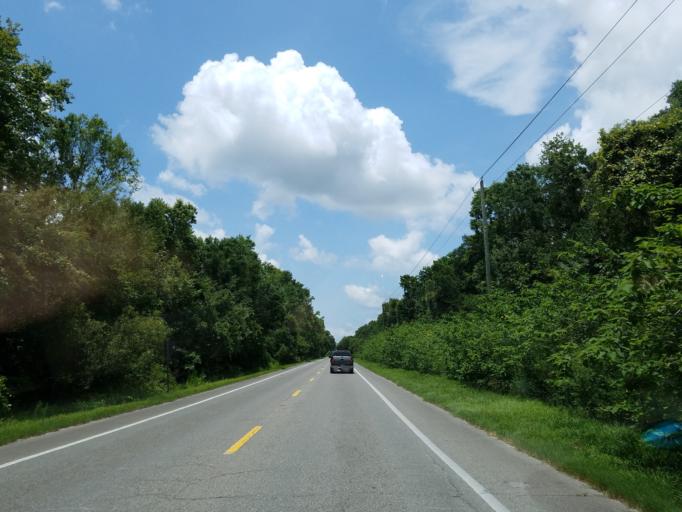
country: US
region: Florida
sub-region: Hillsborough County
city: Fish Hawk
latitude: 27.8506
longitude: -82.1058
